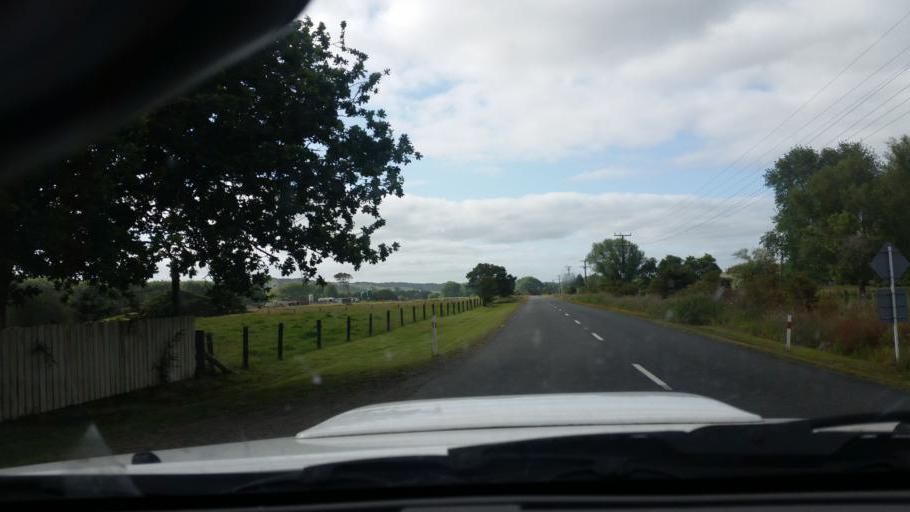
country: NZ
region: Northland
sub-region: Kaipara District
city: Dargaville
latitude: -35.8319
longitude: 173.8417
